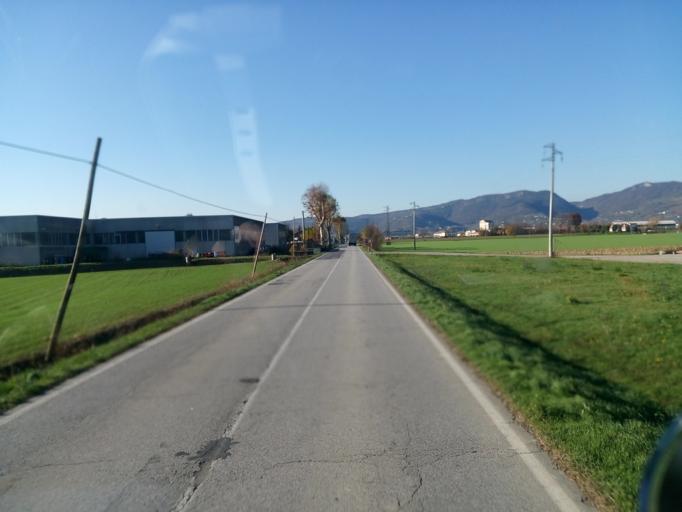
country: IT
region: Veneto
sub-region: Provincia di Vicenza
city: Ponte di Barbarano
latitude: 45.3825
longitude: 11.5793
